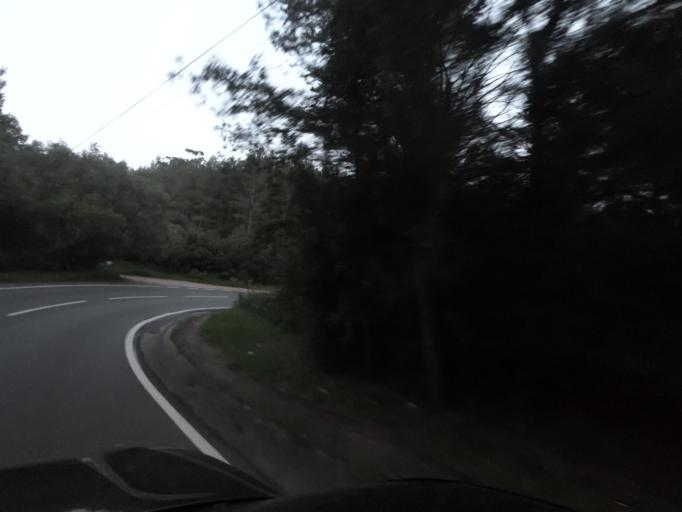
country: PT
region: Setubal
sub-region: Setubal
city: Setubal
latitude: 38.5110
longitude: -8.9228
